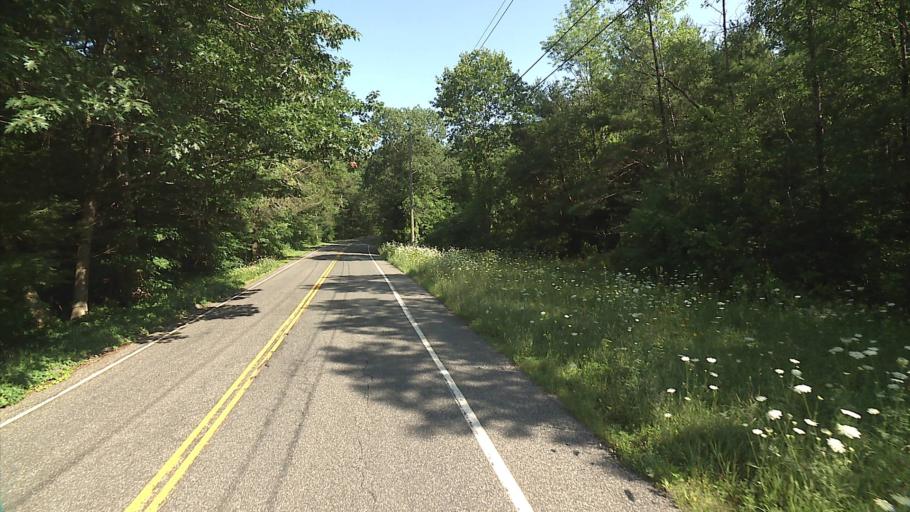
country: US
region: Connecticut
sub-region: Litchfield County
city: Winsted
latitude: 42.0213
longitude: -73.1171
